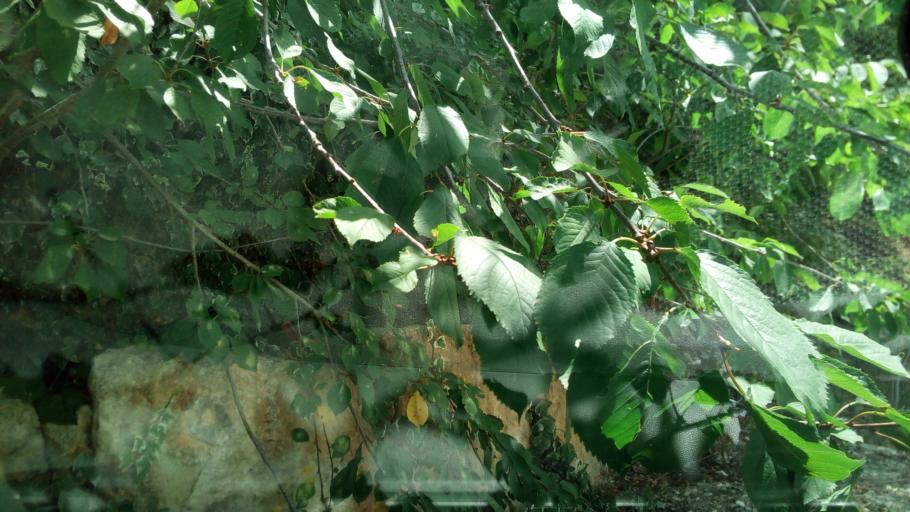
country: CY
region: Pafos
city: Mesogi
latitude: 34.9165
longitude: 32.6320
